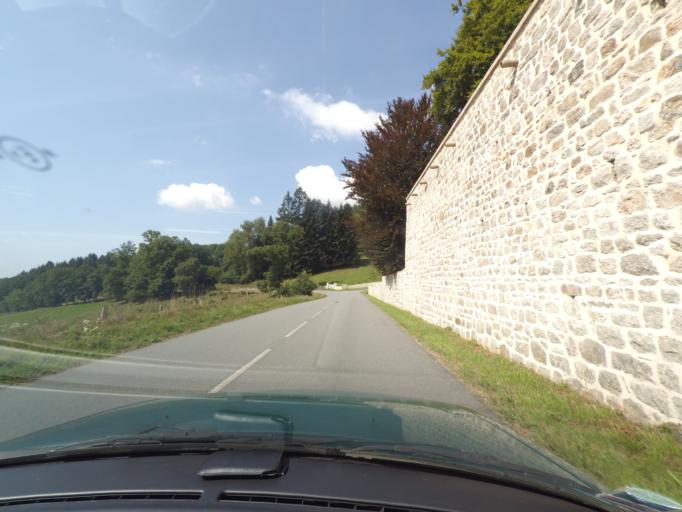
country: FR
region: Limousin
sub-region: Departement de la Haute-Vienne
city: Peyrat-le-Chateau
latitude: 45.7330
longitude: 1.8842
